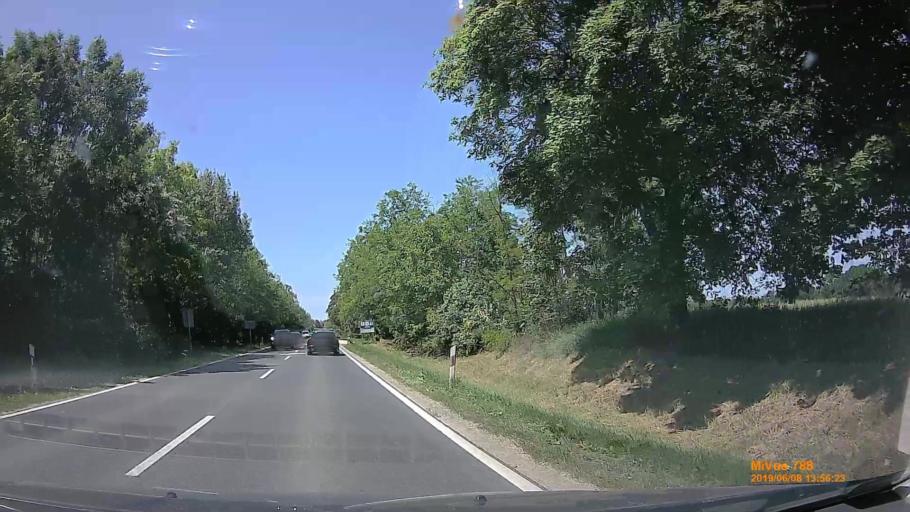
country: HU
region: Vas
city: Sarvar
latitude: 47.3618
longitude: 16.8963
